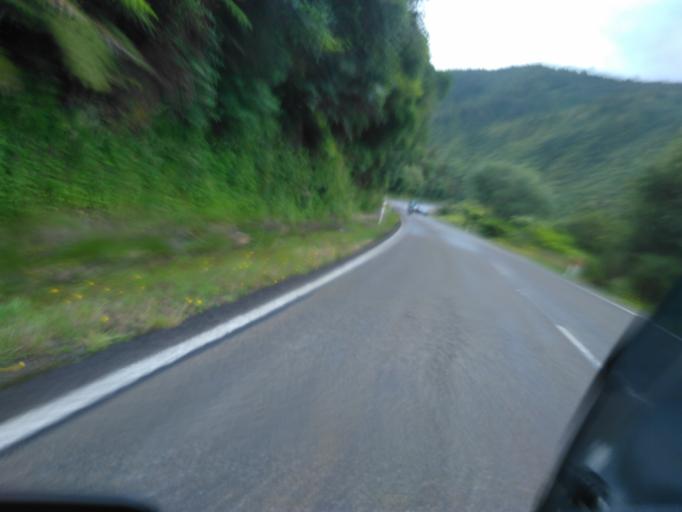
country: NZ
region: Bay of Plenty
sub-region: Opotiki District
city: Opotiki
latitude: -38.2432
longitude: 177.3095
